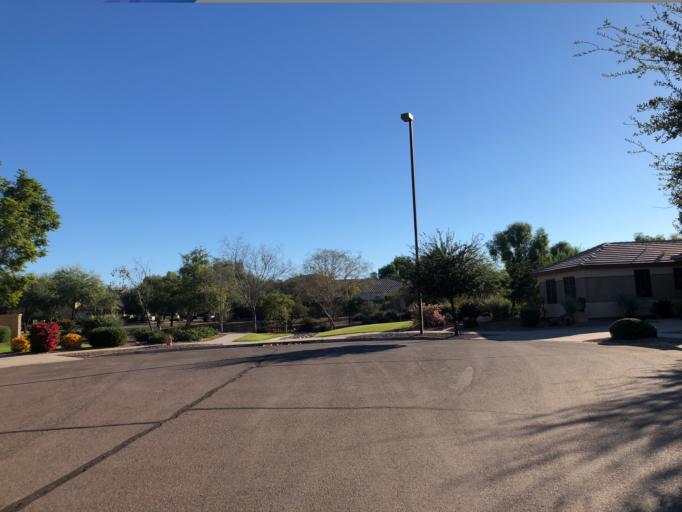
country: US
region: Arizona
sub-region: Maricopa County
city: Queen Creek
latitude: 33.2775
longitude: -111.6952
